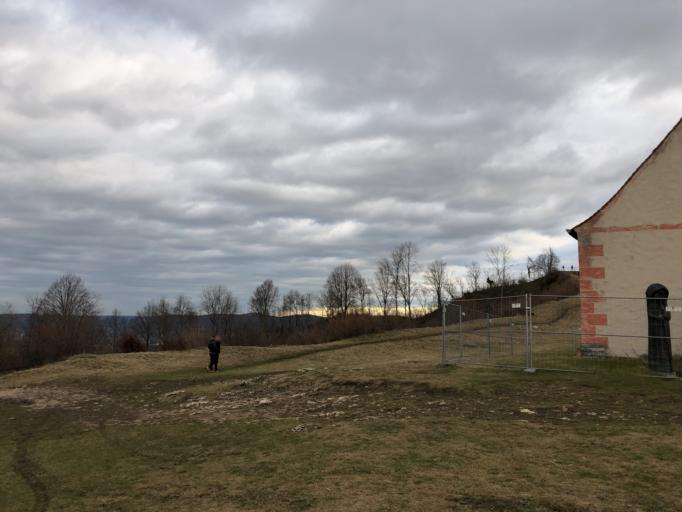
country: DE
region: Bavaria
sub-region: Upper Franconia
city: Kirchehrenbach
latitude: 49.7205
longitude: 11.1526
